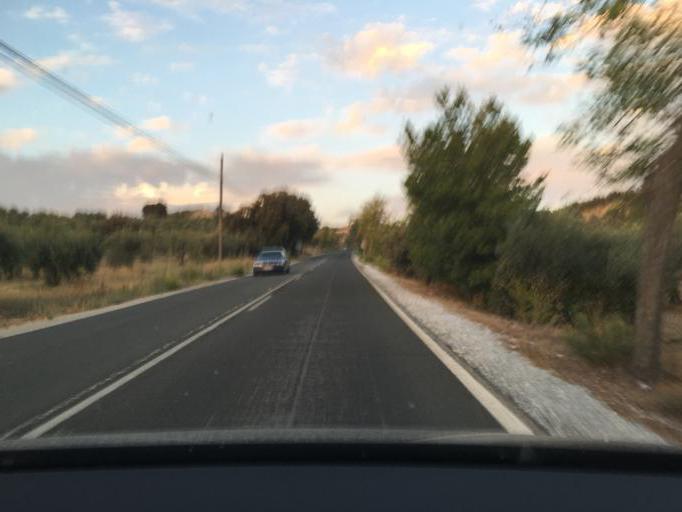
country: ES
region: Andalusia
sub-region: Provincia de Granada
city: Viznar
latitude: 37.2136
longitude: -3.5494
